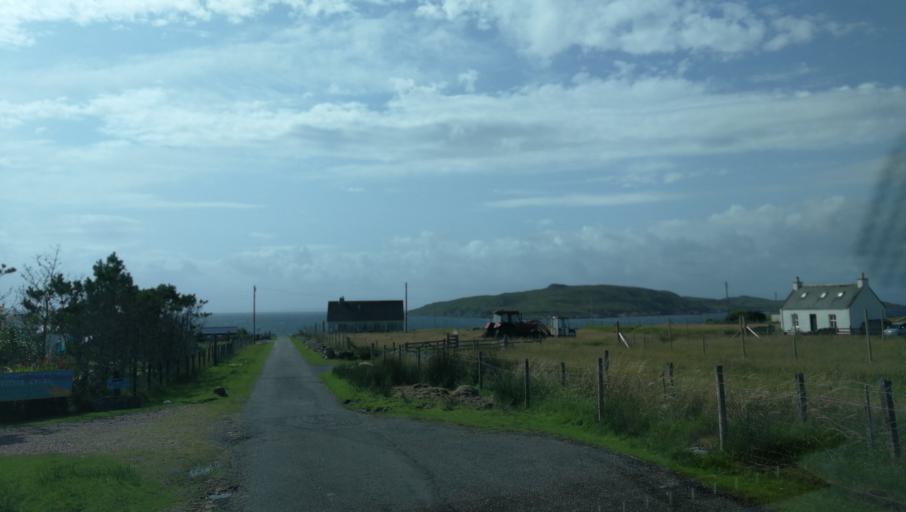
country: GB
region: Scotland
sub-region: Highland
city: Portree
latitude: 57.7439
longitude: -5.7761
